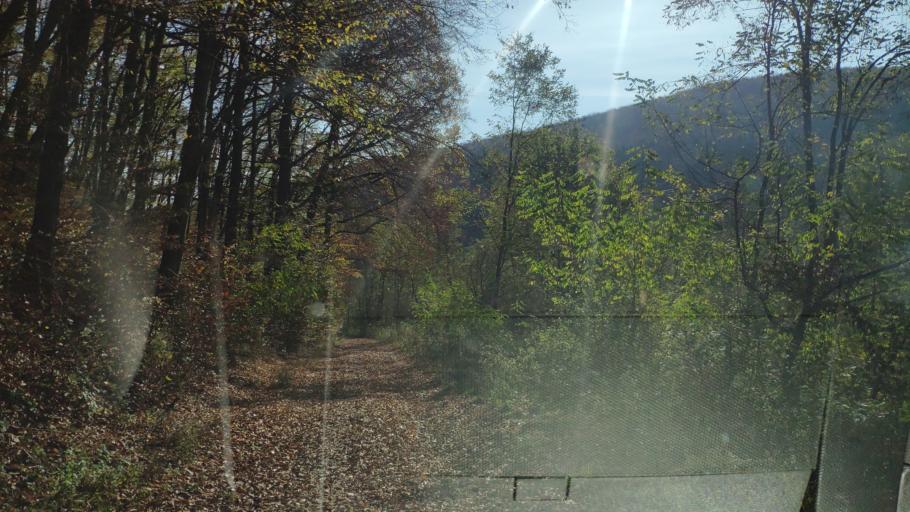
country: SK
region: Presovsky
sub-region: Okres Presov
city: Presov
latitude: 48.9028
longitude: 21.2252
